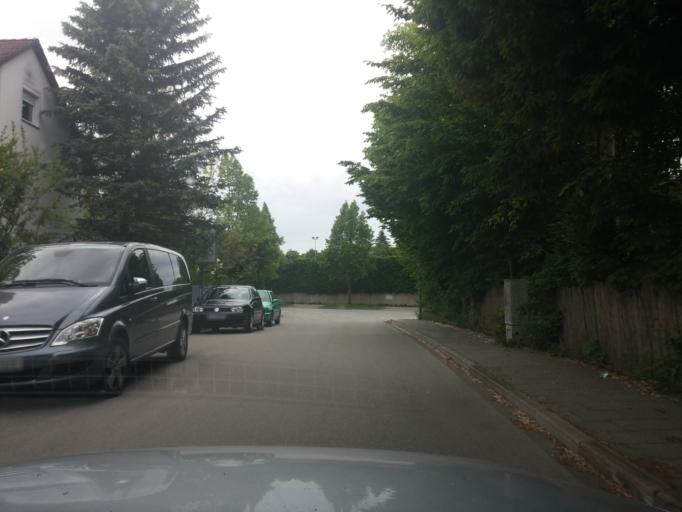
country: DE
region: Bavaria
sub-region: Upper Bavaria
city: Haar
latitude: 48.1081
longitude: 11.7390
